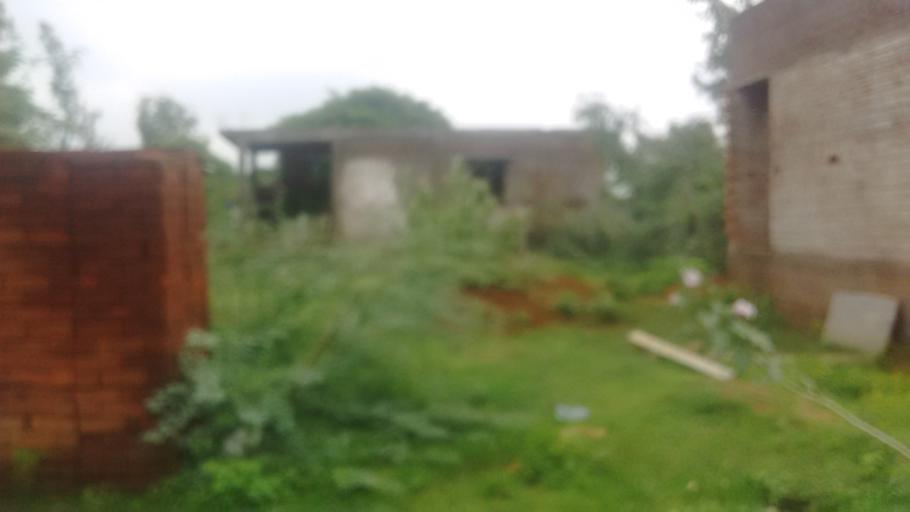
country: IN
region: Tamil Nadu
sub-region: Kancheepuram
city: Madambakkam
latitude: 12.8958
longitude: 80.0321
